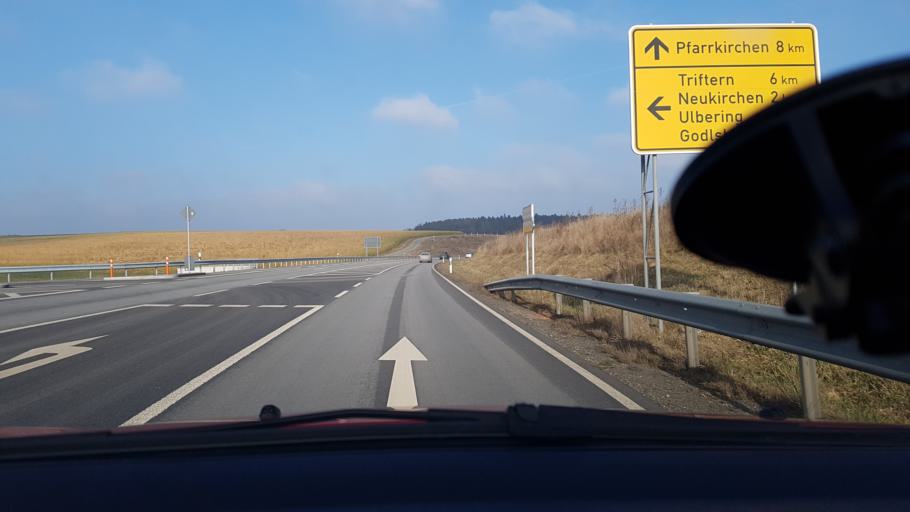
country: DE
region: Bavaria
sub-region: Lower Bavaria
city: Wittibreut
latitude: 48.3726
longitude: 12.9534
